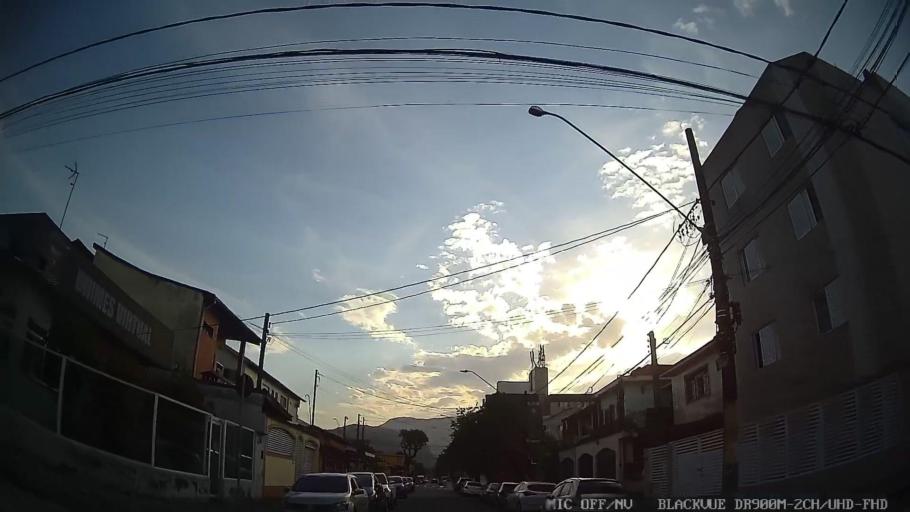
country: BR
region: Sao Paulo
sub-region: Cubatao
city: Cubatao
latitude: -23.8942
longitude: -46.4245
